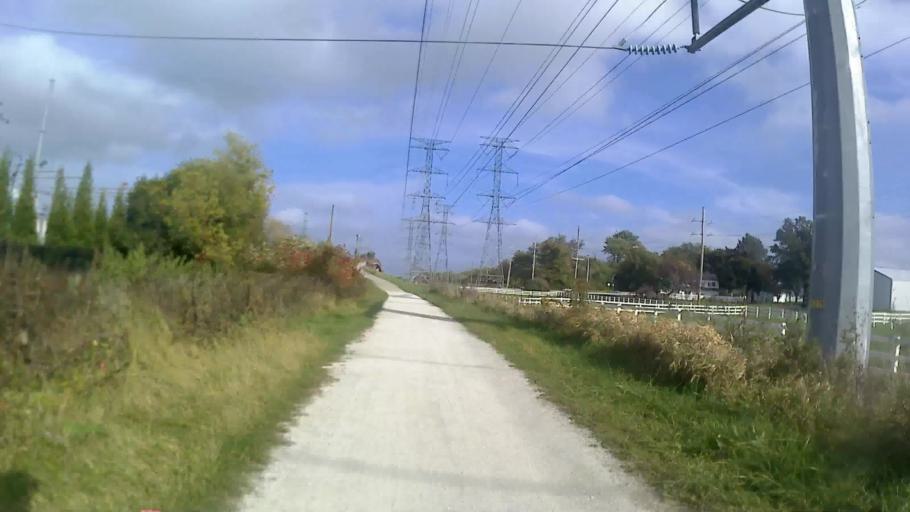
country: US
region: Illinois
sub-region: DuPage County
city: Warrenville
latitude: 41.7950
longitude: -88.2425
